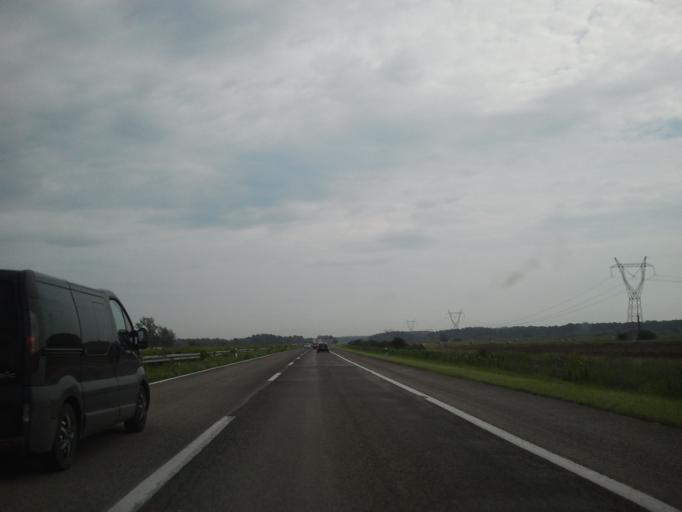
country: HR
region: Zagrebacka
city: Jastrebarsko
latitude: 45.6311
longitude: 15.6611
